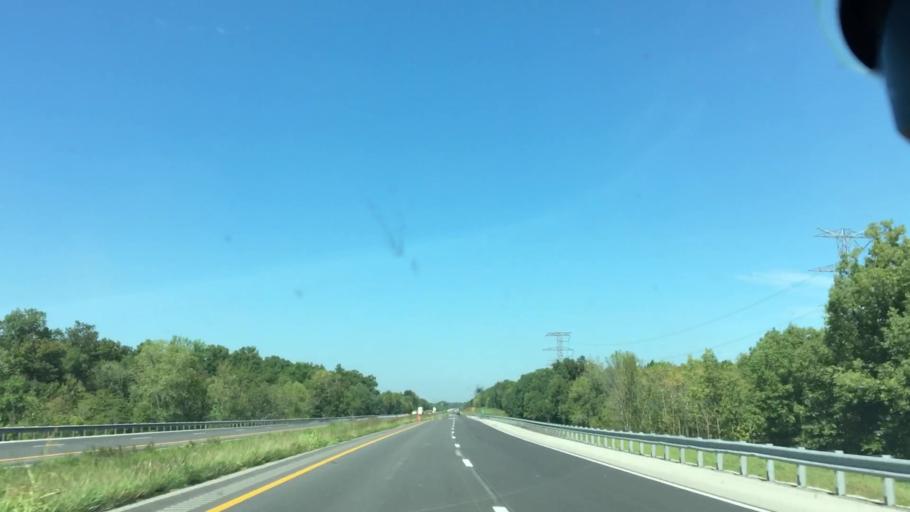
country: US
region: Kentucky
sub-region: Webster County
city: Sebree
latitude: 37.6280
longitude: -87.5083
